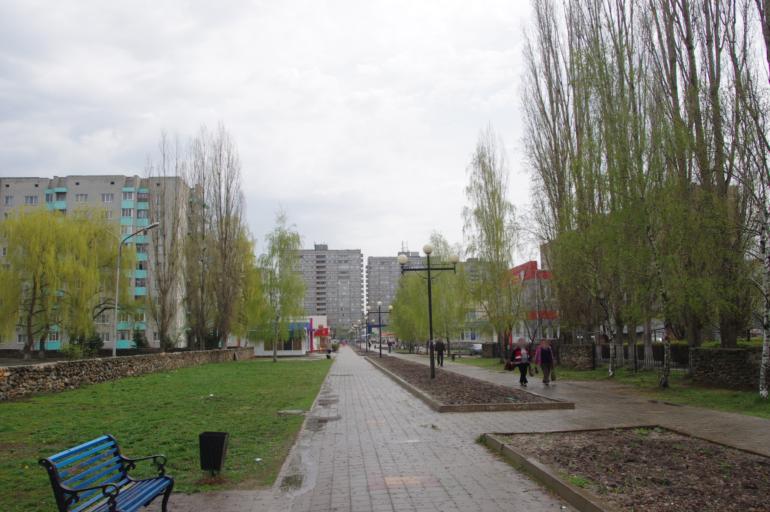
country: RU
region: Kursk
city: Kurchatov
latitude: 51.6554
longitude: 35.6783
